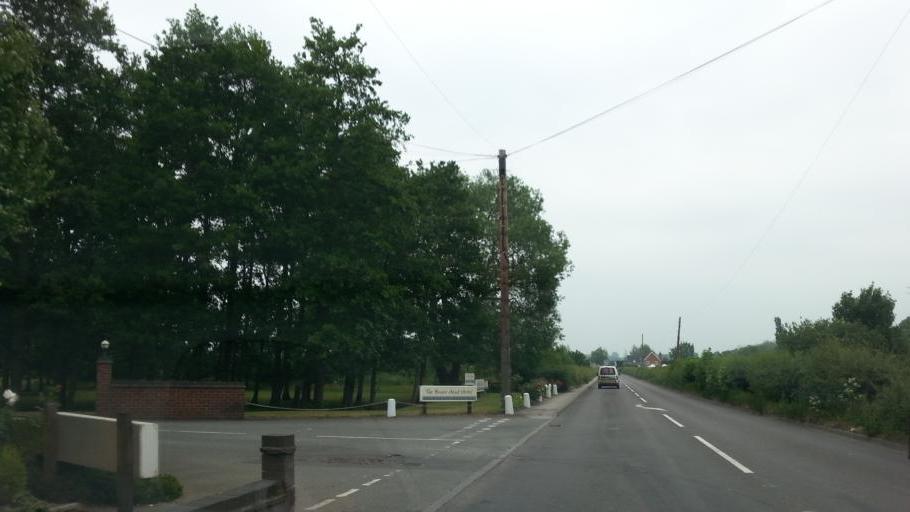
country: GB
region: England
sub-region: Derbyshire
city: Rodsley
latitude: 52.8739
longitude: -1.7600
